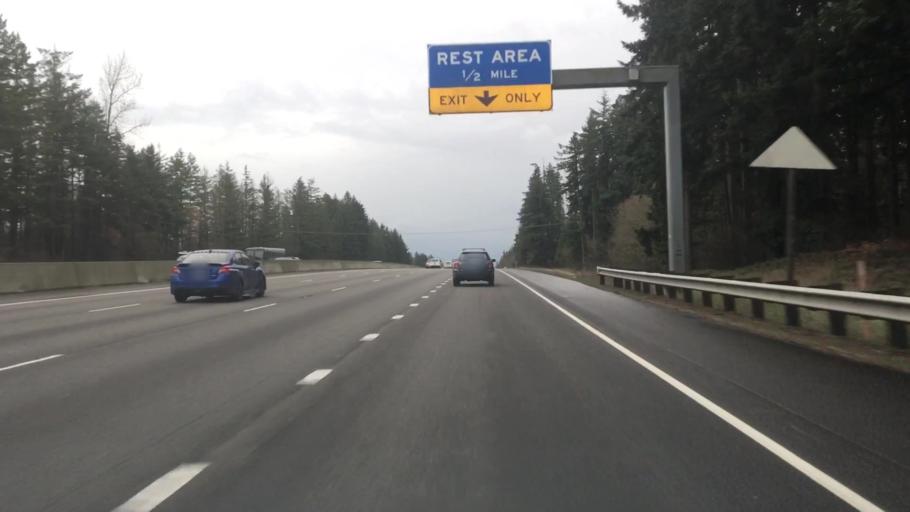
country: US
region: Washington
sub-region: Thurston County
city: Grand Mound
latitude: 46.8818
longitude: -122.9659
